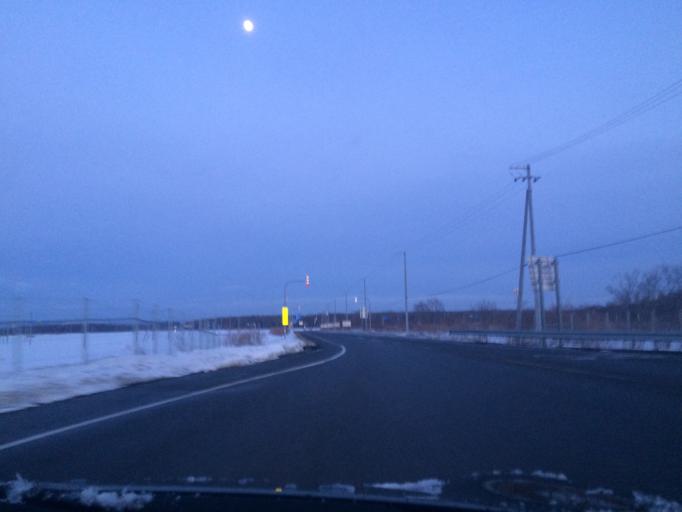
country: JP
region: Hokkaido
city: Chitose
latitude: 42.7766
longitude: 141.6329
